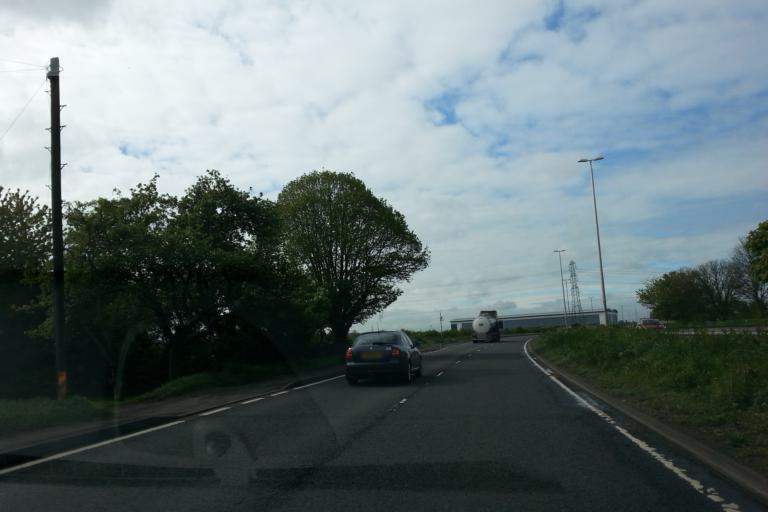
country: GB
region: England
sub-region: Staffordshire
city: Barton under Needwood
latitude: 52.7779
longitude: -1.6825
